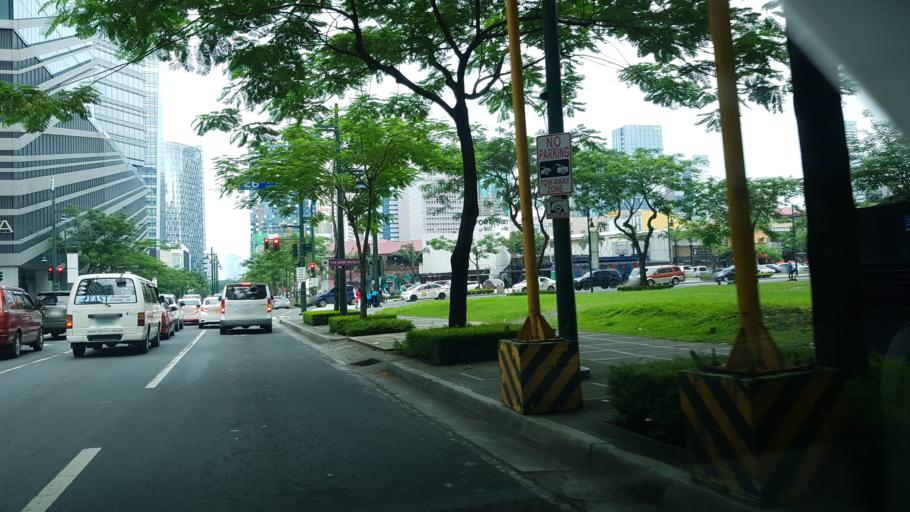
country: PH
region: Metro Manila
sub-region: Makati City
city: Makati City
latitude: 14.5484
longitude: 121.0466
